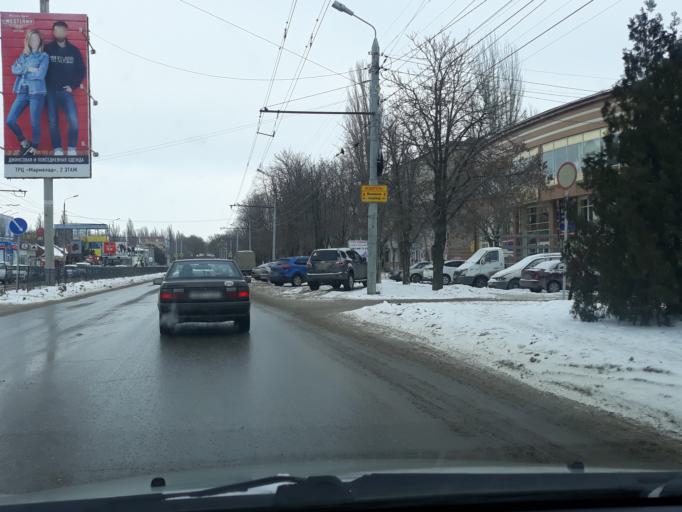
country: RU
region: Rostov
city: Taganrog
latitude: 47.2500
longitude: 38.9179
